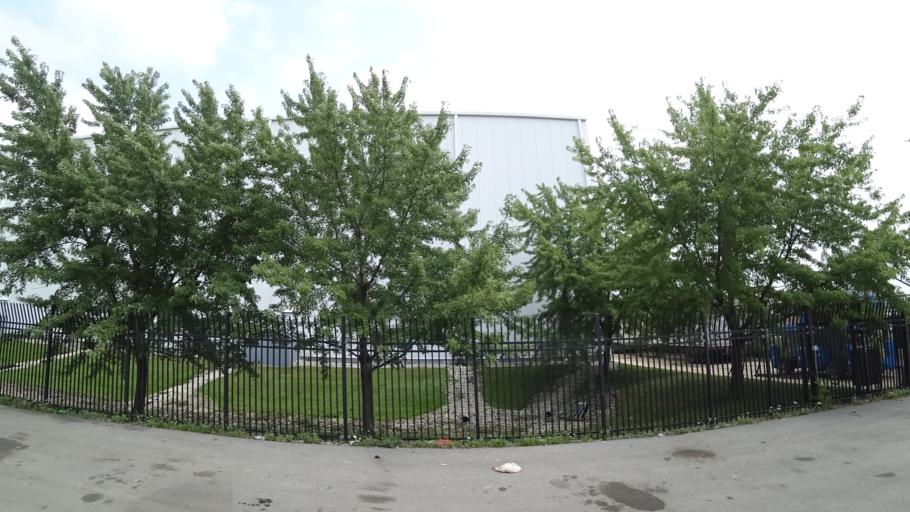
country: US
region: Illinois
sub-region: Cook County
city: Chicago
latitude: 41.8458
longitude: -87.6781
